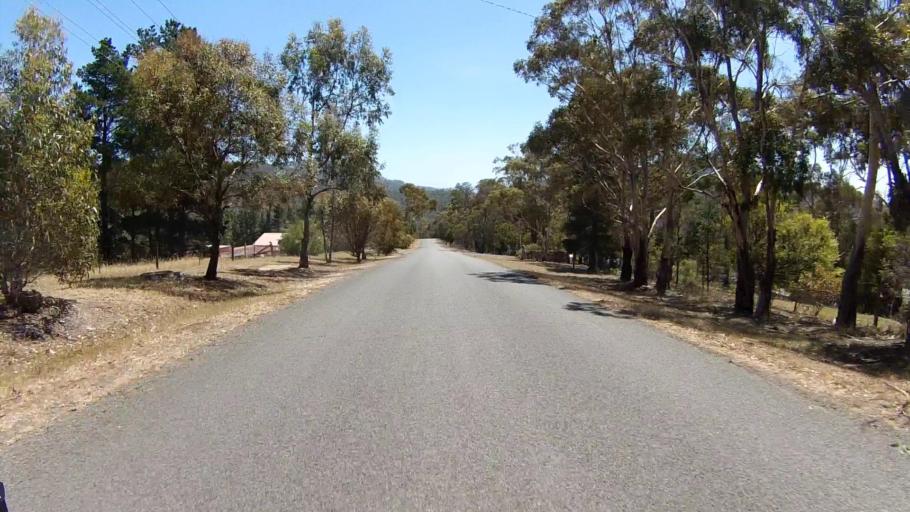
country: AU
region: Tasmania
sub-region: Clarence
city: Cambridge
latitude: -42.8473
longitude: 147.4241
